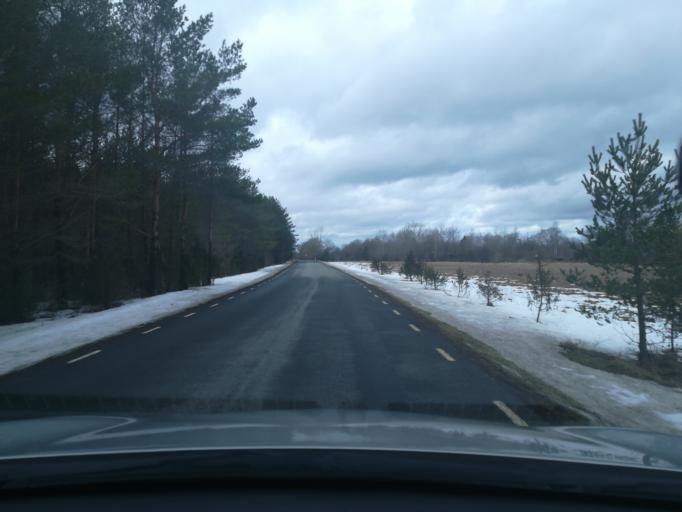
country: EE
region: Harju
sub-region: Saue linn
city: Saue
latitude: 59.3606
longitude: 24.5236
